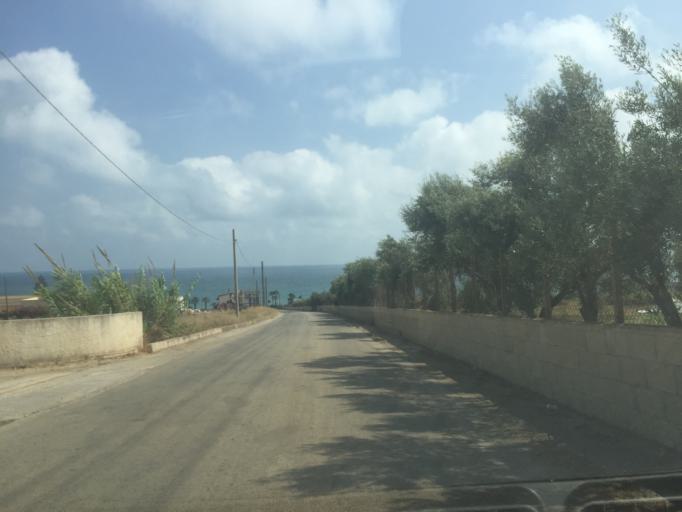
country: IT
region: Sicily
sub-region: Ragusa
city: Donnalucata
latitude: 36.7685
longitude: 14.6279
